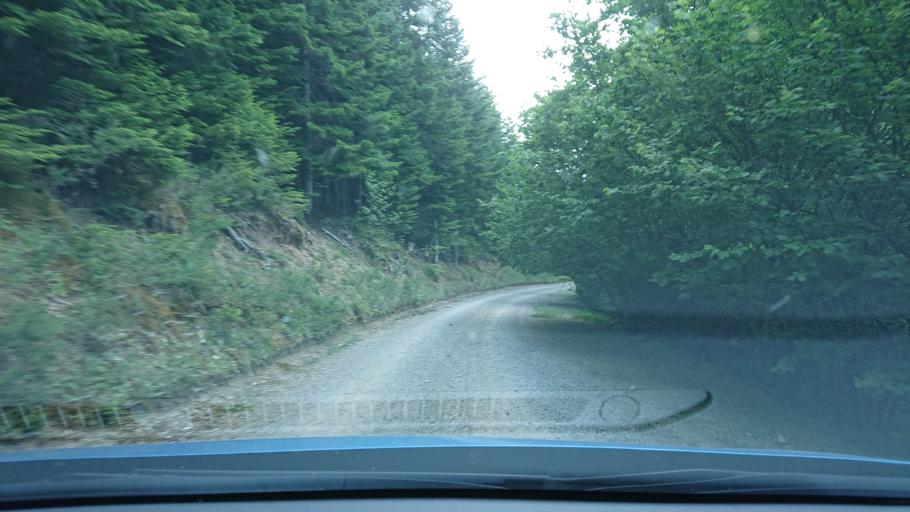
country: FR
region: Rhone-Alpes
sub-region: Departement de l'Isere
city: Mens
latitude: 44.7990
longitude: 5.8906
